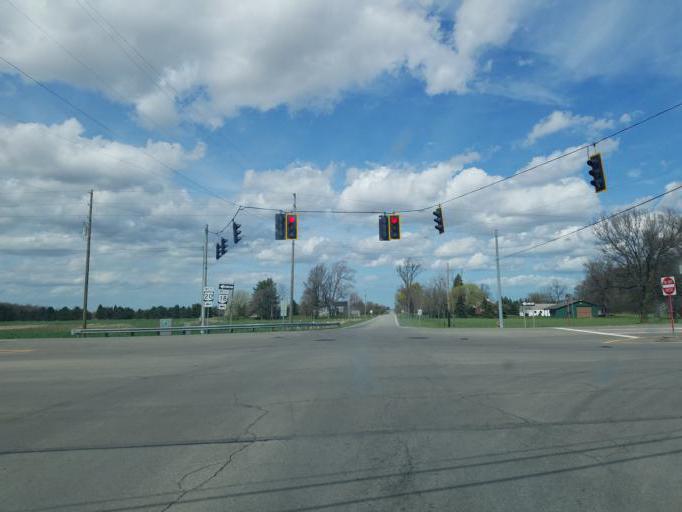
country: US
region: Ohio
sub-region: Huron County
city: Bellevue
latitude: 41.2651
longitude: -82.7948
